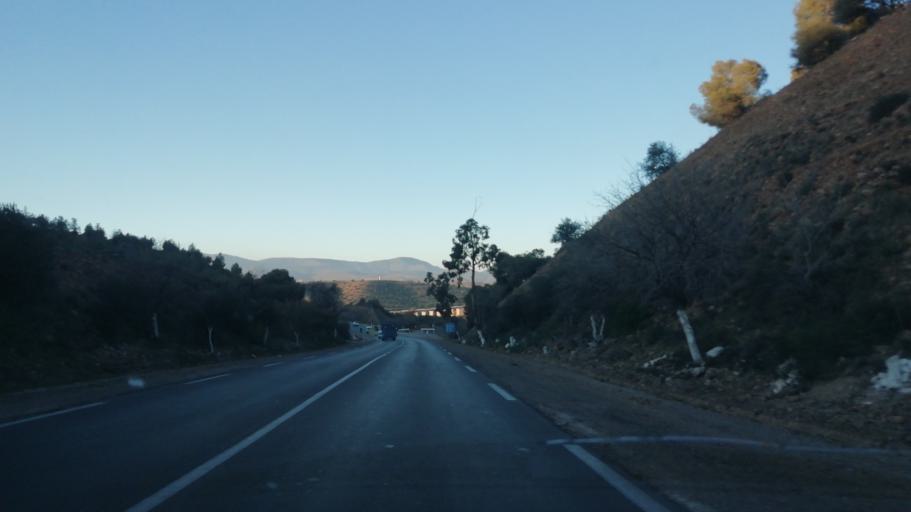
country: DZ
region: Tlemcen
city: Nedroma
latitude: 34.8770
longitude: -1.6683
